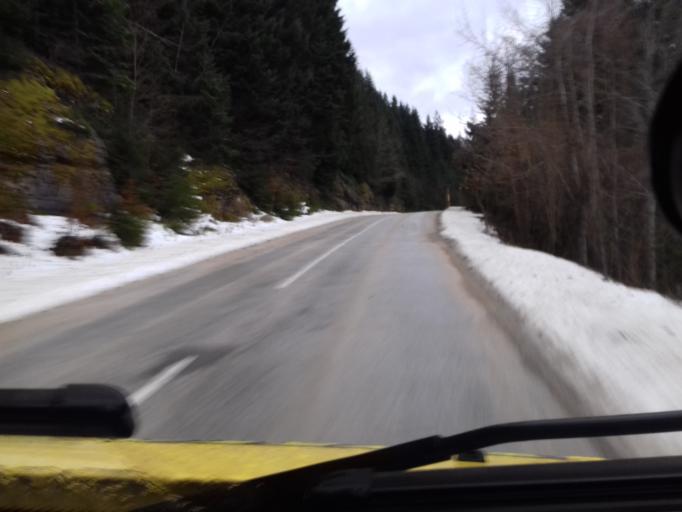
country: BA
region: Federation of Bosnia and Herzegovina
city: Turbe
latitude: 44.3163
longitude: 17.5085
